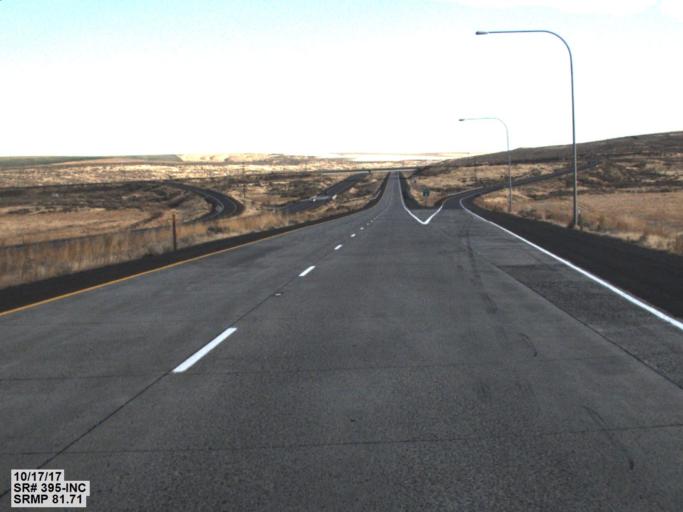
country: US
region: Washington
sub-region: Adams County
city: Ritzville
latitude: 46.9637
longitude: -118.5712
